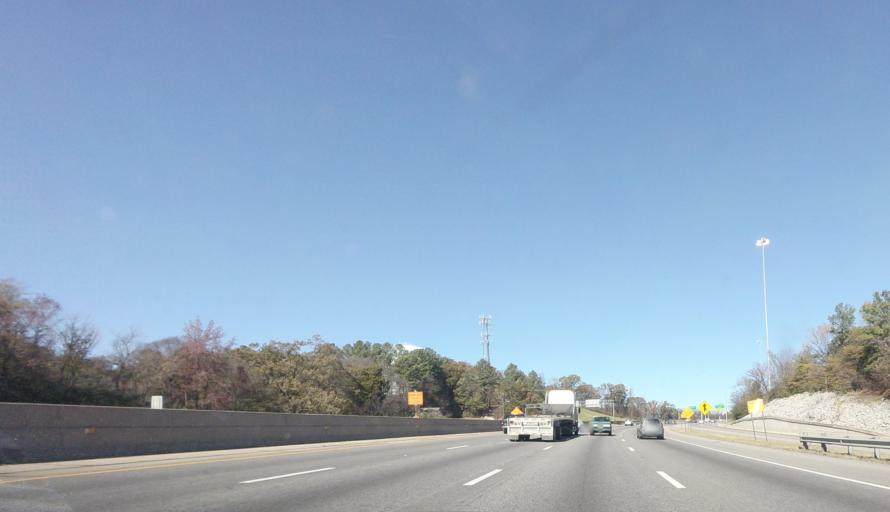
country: US
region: Alabama
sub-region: Jefferson County
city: Birmingham
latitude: 33.5537
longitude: -86.8308
